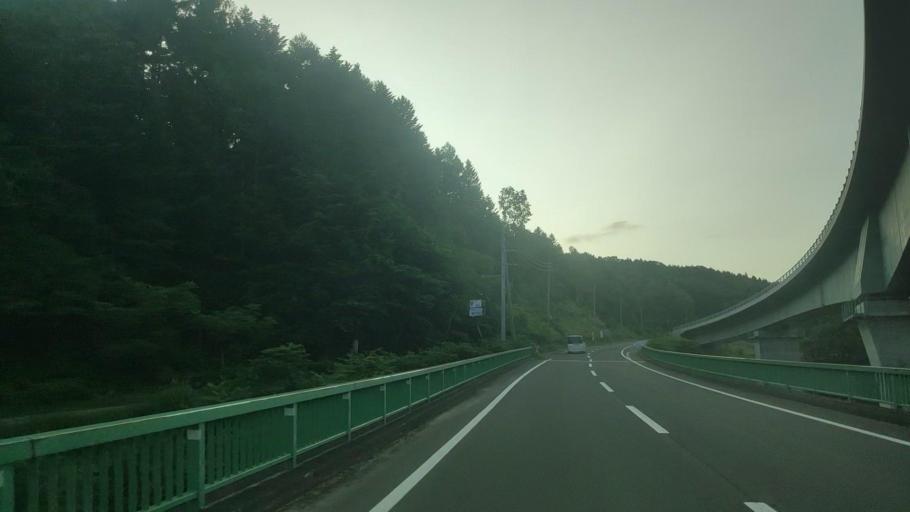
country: JP
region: Hokkaido
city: Bibai
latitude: 43.2275
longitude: 142.0431
